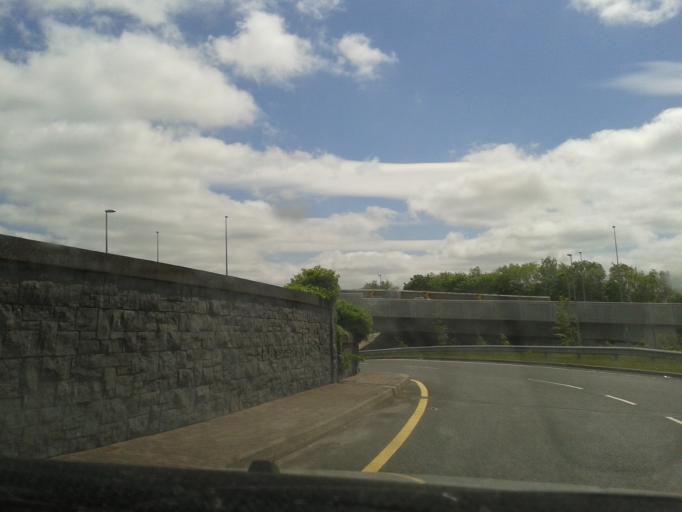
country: IE
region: Leinster
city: Castleknock
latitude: 53.3825
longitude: -6.3617
